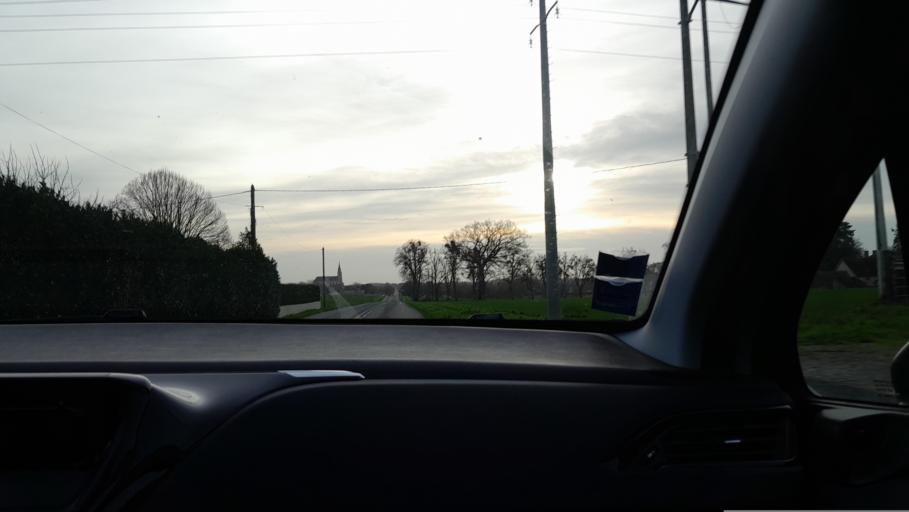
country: FR
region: Pays de la Loire
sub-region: Departement de la Mayenne
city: Craon
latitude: 47.8551
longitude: -0.9671
